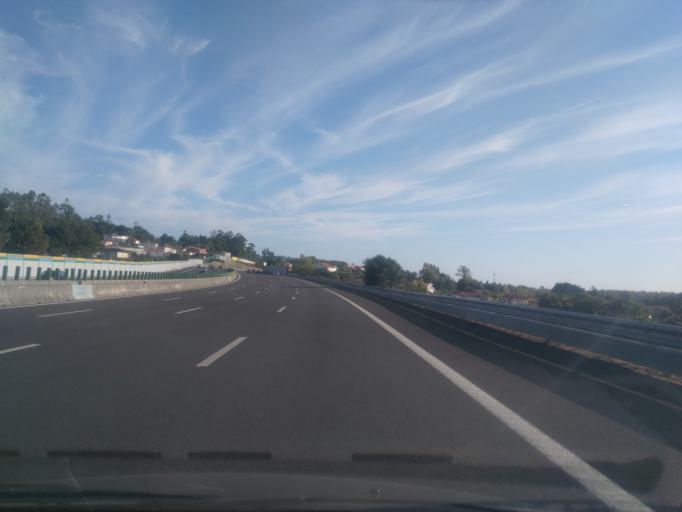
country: PT
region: Porto
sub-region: Vila Nova de Gaia
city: Grijo
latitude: 41.0344
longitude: -8.5723
